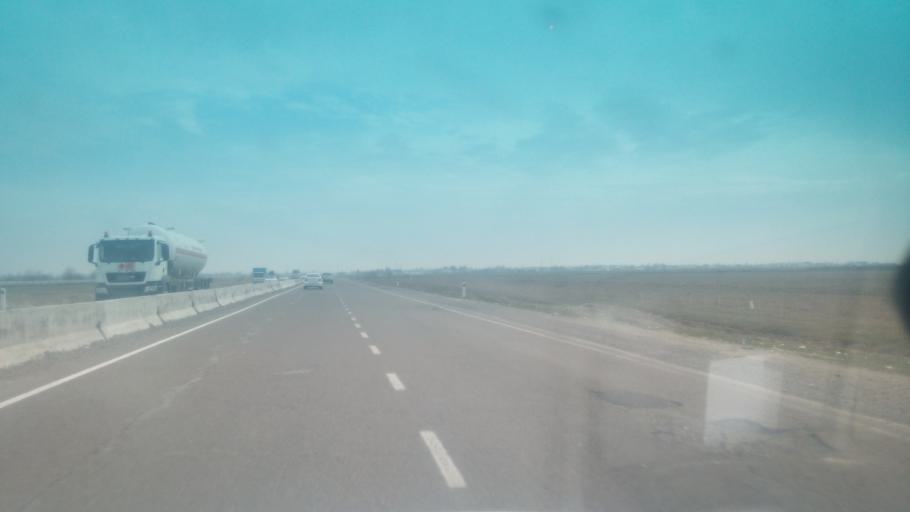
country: KZ
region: Ongtustik Qazaqstan
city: Myrzakent
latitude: 40.5117
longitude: 68.4946
